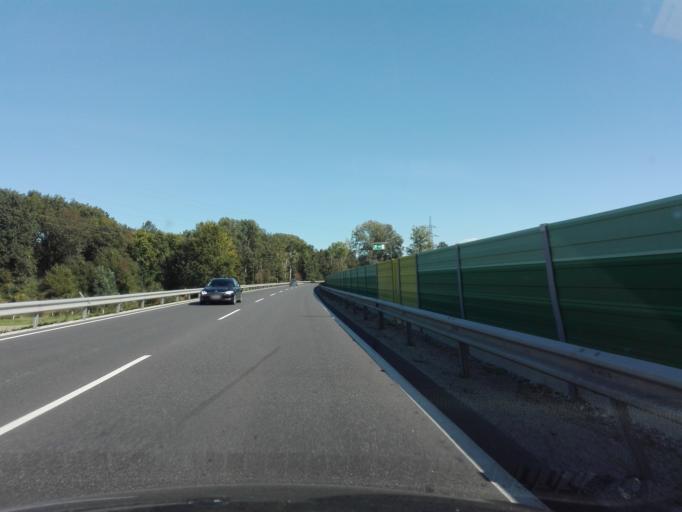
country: AT
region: Lower Austria
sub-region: Politischer Bezirk Amstetten
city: Ennsdorf
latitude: 48.2337
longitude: 14.5236
